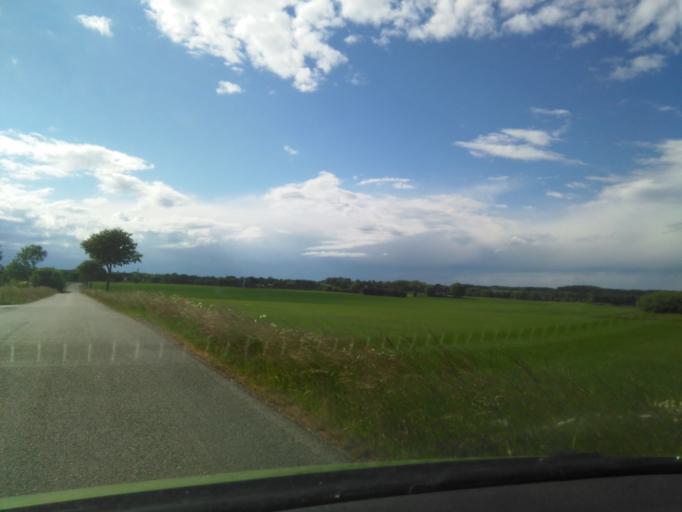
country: DK
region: Capital Region
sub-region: Bornholm Kommune
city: Nexo
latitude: 55.1257
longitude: 15.0574
